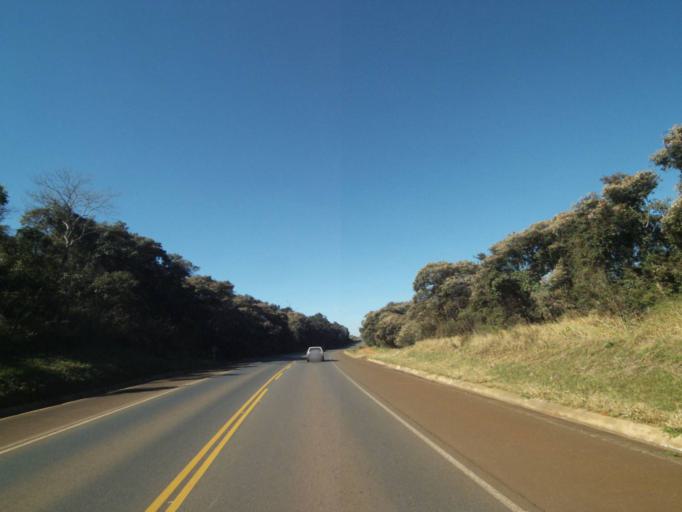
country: BR
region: Parana
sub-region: Tibagi
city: Tibagi
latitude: -24.4225
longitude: -50.3848
